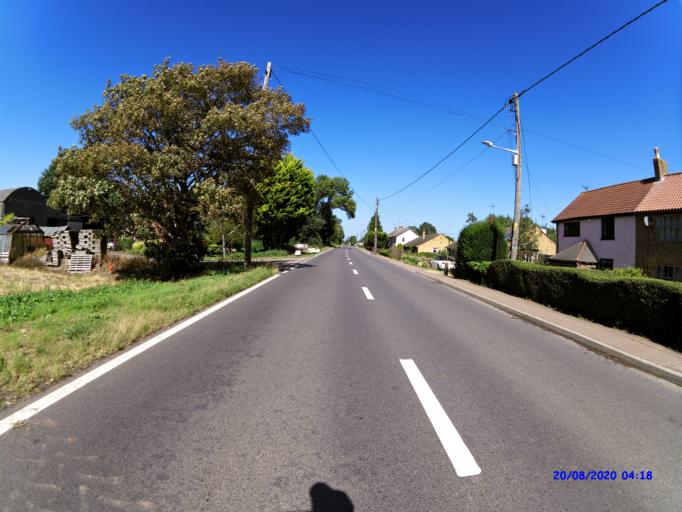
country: GB
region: England
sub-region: Cambridgeshire
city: Ramsey
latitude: 52.4901
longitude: -0.1156
